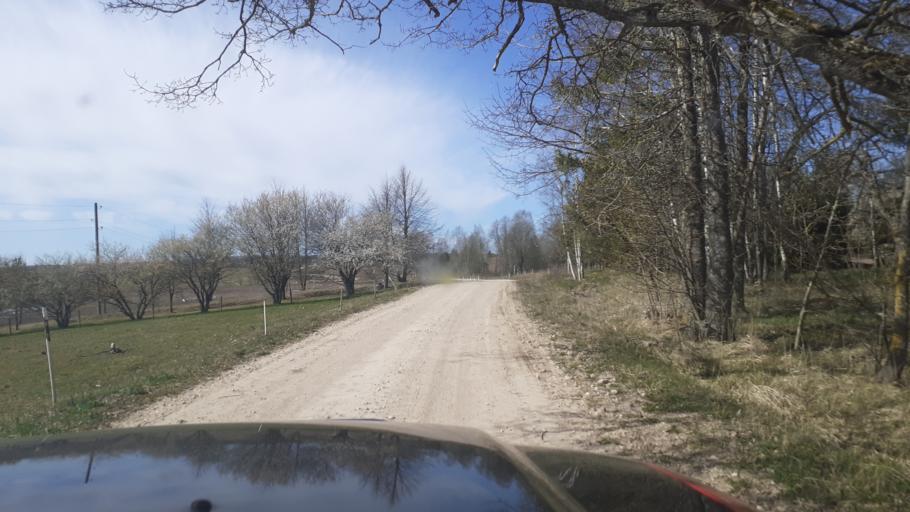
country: LV
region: Kuldigas Rajons
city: Kuldiga
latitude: 56.8364
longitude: 22.0000
